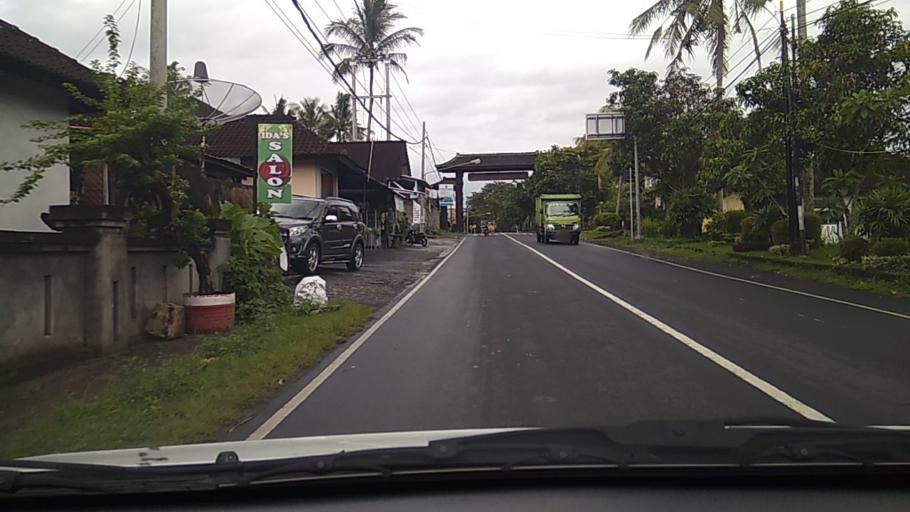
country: ID
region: Bali
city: Banjar Budakeling
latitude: -8.4341
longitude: 115.5901
